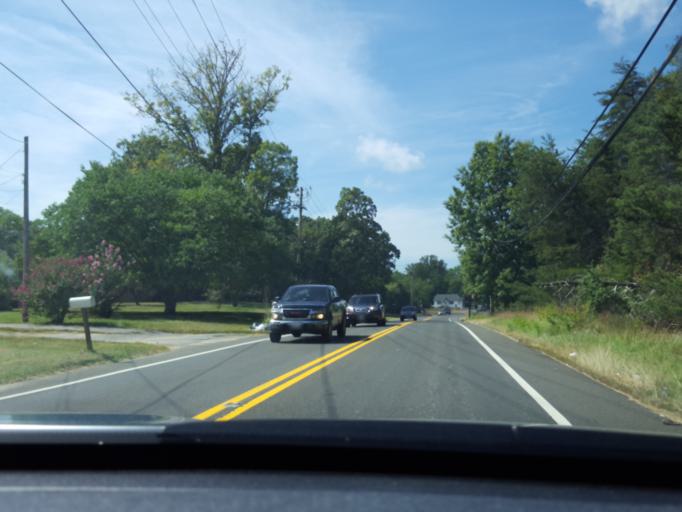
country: US
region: Maryland
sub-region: Prince George's County
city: Andrews AFB
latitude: 38.7767
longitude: -76.8641
